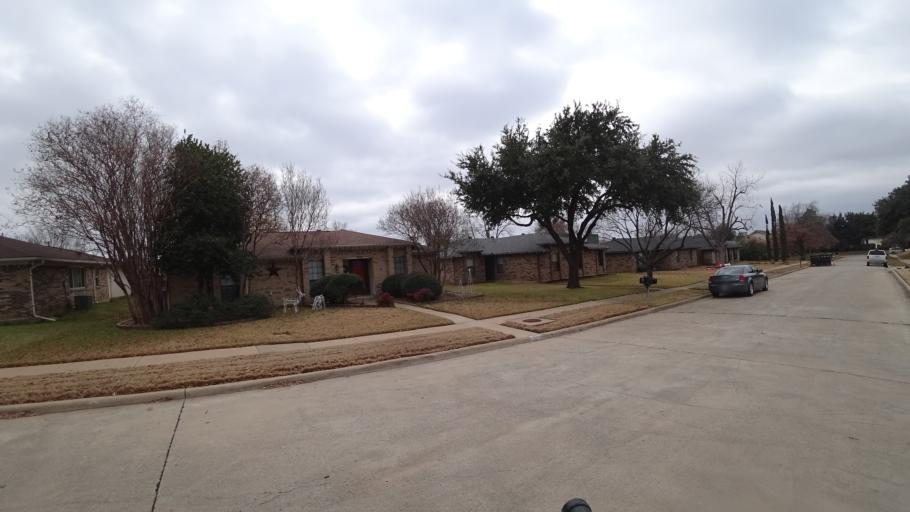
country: US
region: Texas
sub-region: Denton County
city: Highland Village
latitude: 33.0479
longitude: -97.0424
